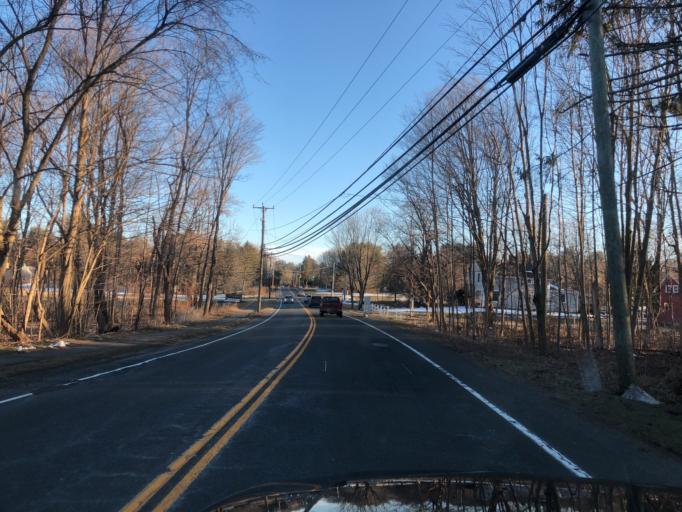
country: US
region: Connecticut
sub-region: Hartford County
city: Canton Valley
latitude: 41.7770
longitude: -72.8632
